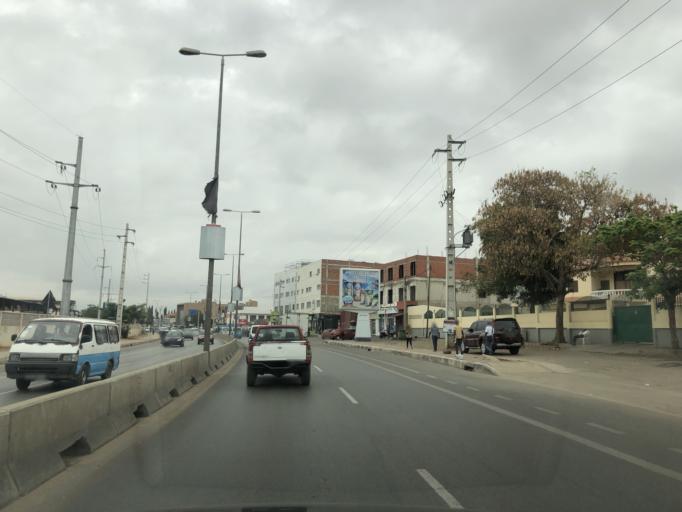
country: AO
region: Luanda
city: Luanda
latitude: -8.8948
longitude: 13.1921
